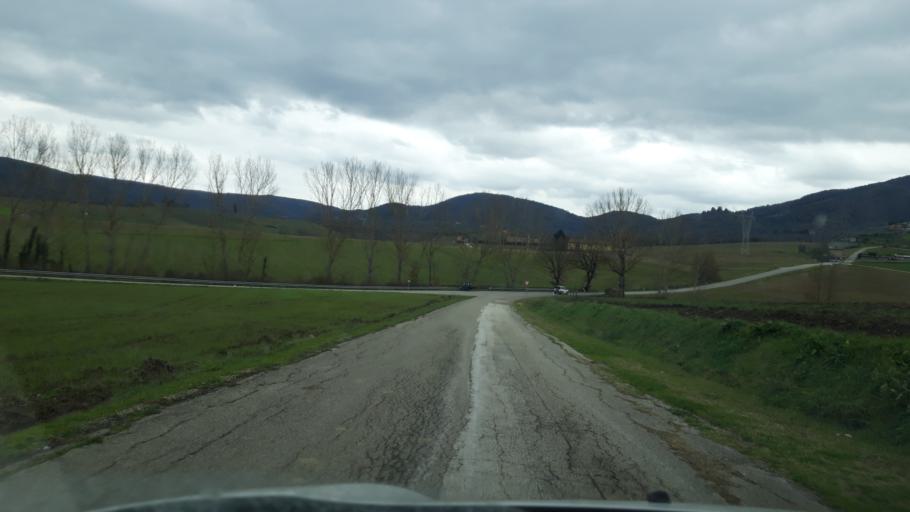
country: IT
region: Umbria
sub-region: Provincia di Perugia
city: Fontignano
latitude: 42.9910
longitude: 12.1808
